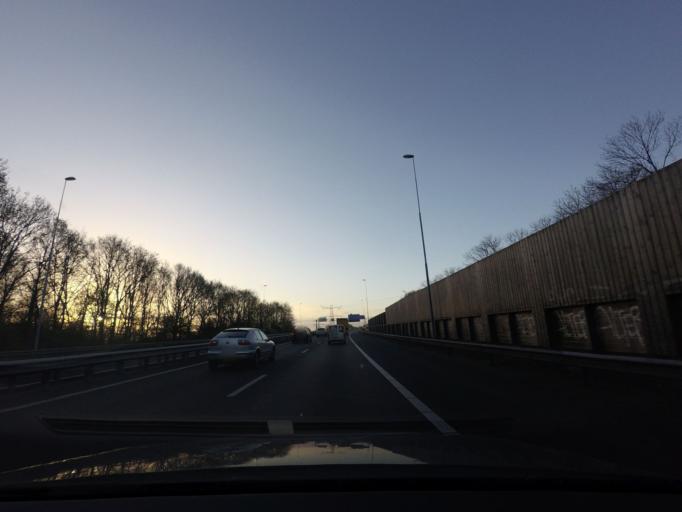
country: NL
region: North Holland
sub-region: Gemeente Zaanstad
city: Zaanstad
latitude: 52.4602
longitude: 4.8323
